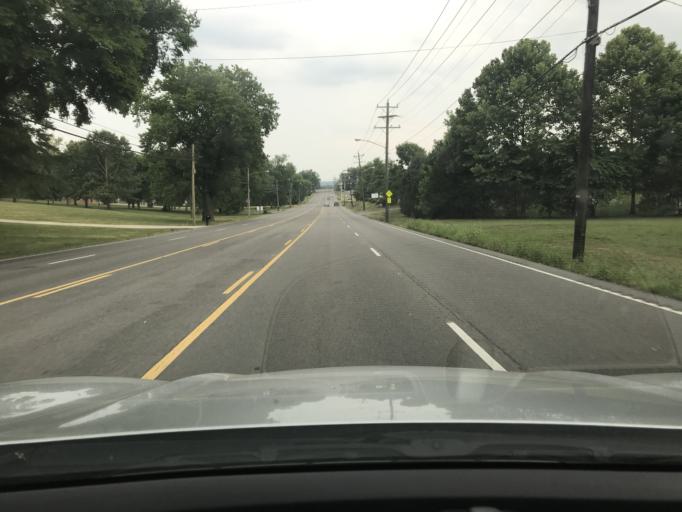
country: US
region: Tennessee
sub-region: Davidson County
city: Goodlettsville
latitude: 36.3084
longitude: -86.7172
